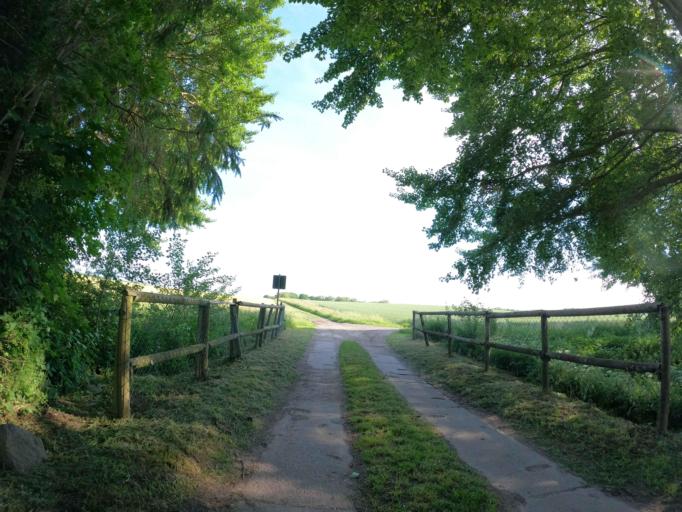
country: DE
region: Mecklenburg-Vorpommern
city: Preetz
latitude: 54.3285
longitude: 12.9737
